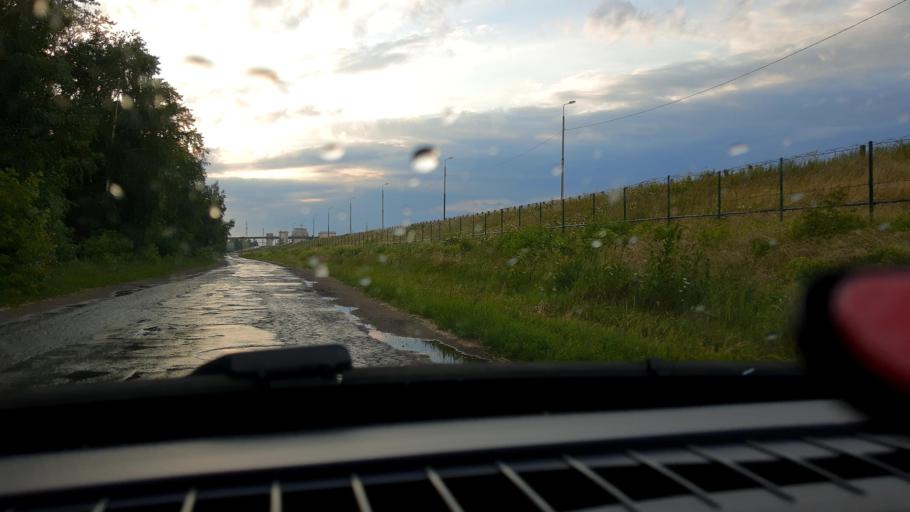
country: RU
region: Nizjnij Novgorod
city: Zavolzh'ye
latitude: 56.6699
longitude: 43.4273
